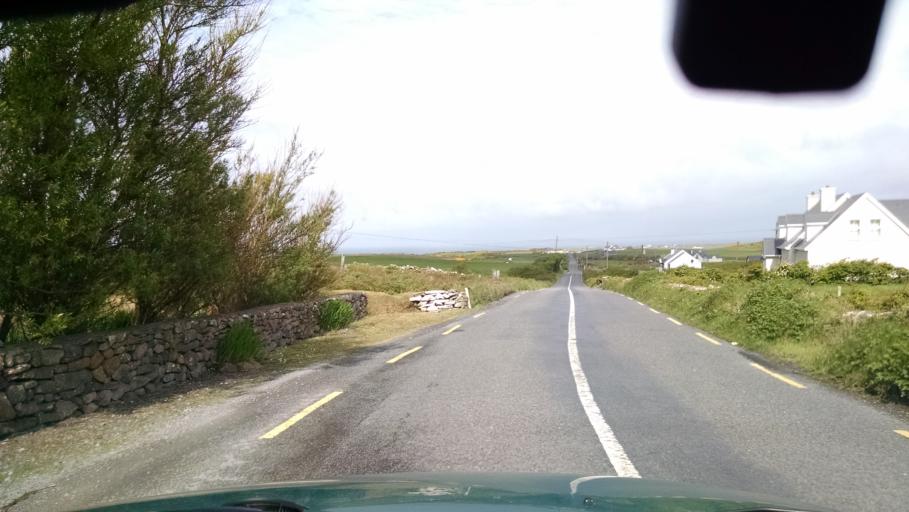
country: IE
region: Connaught
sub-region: County Galway
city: Bearna
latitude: 53.0092
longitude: -9.3595
